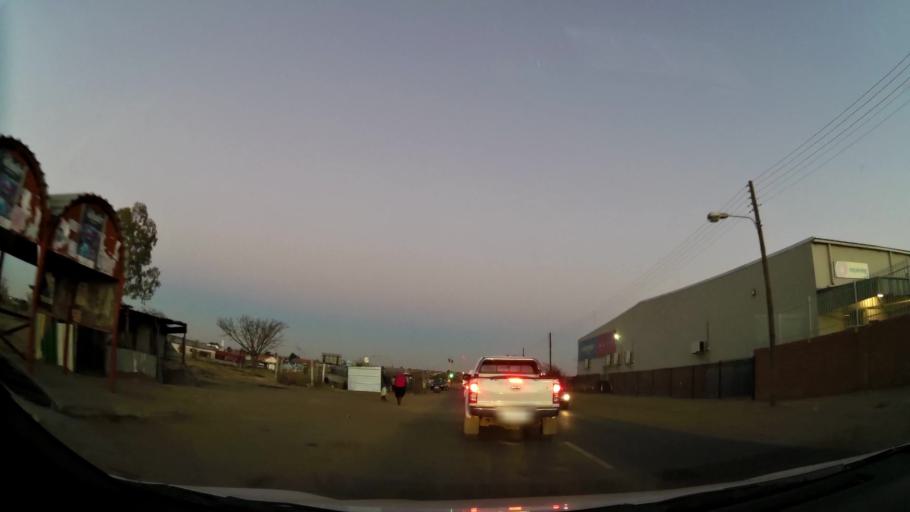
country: ZA
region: Limpopo
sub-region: Capricorn District Municipality
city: Polokwane
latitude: -23.8515
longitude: 29.3997
